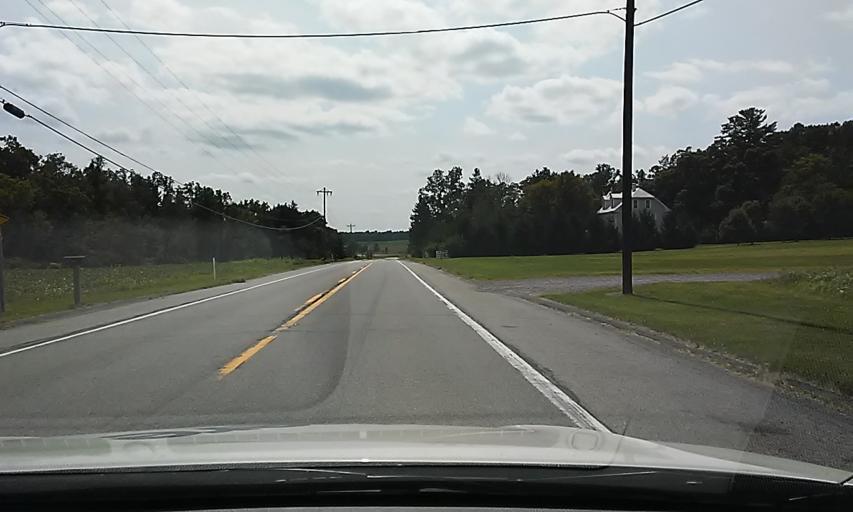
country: US
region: Pennsylvania
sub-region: Jefferson County
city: Punxsutawney
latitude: 40.8448
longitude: -79.0392
